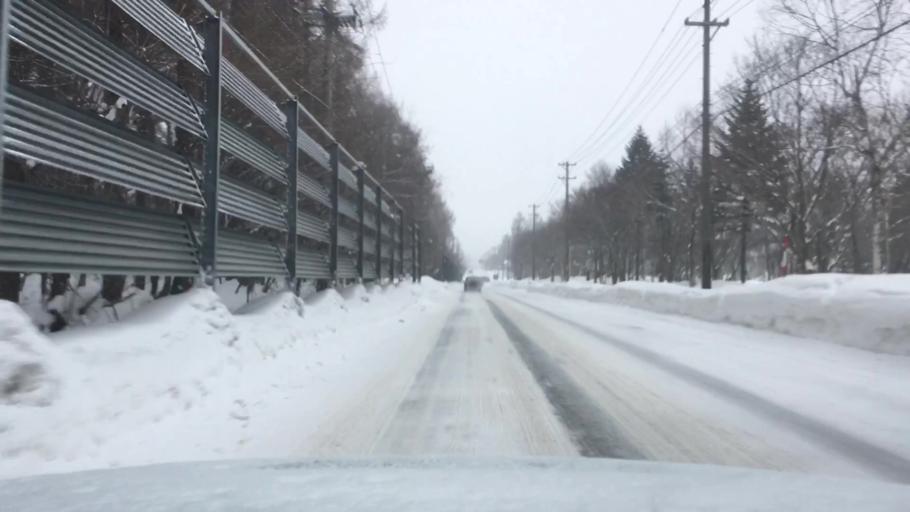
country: JP
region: Akita
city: Hanawa
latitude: 40.0071
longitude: 140.9742
